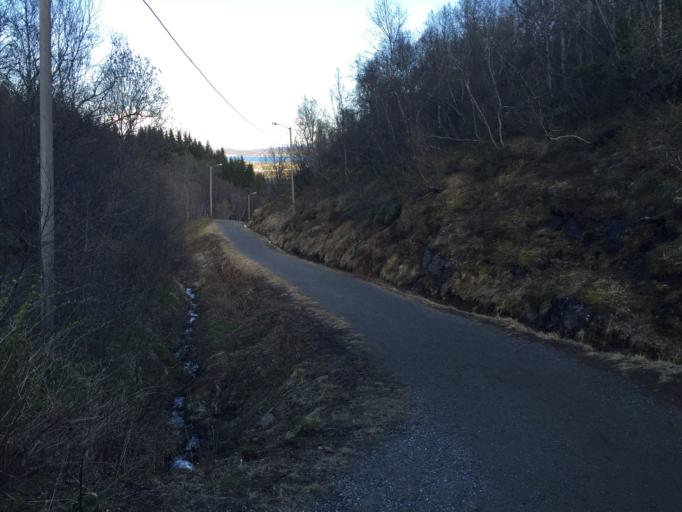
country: NO
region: Nordland
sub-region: Bodo
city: Lopsmarka
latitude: 67.2898
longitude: 14.5406
